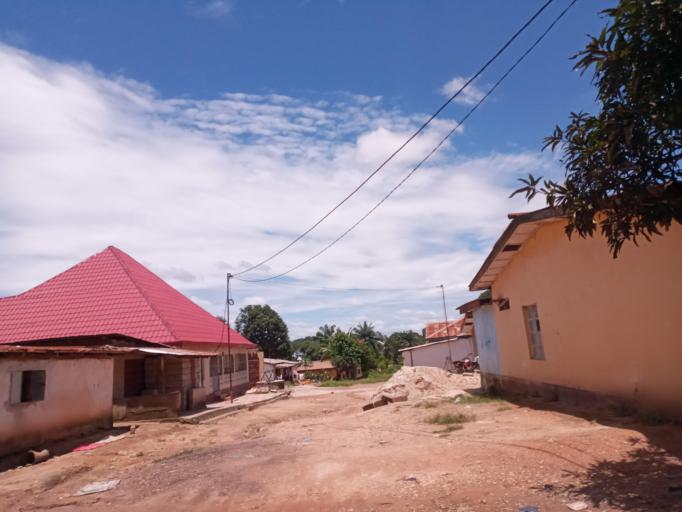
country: SL
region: Eastern Province
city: Koidu
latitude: 8.6415
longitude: -10.9632
